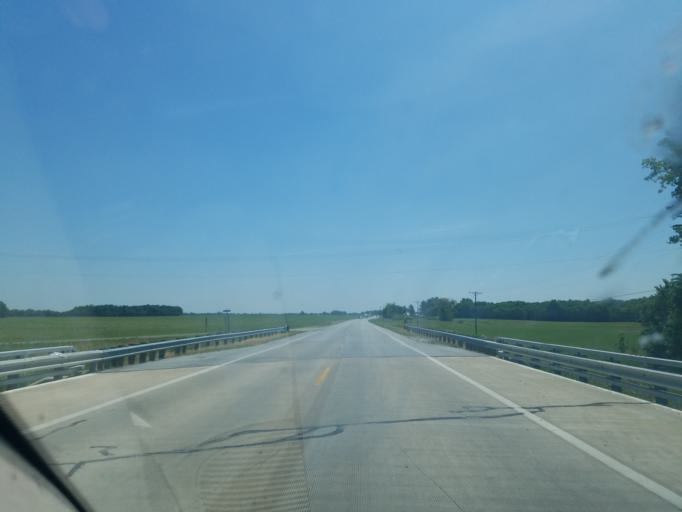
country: US
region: Ohio
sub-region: Mercer County
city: Rockford
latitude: 40.7265
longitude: -84.7379
